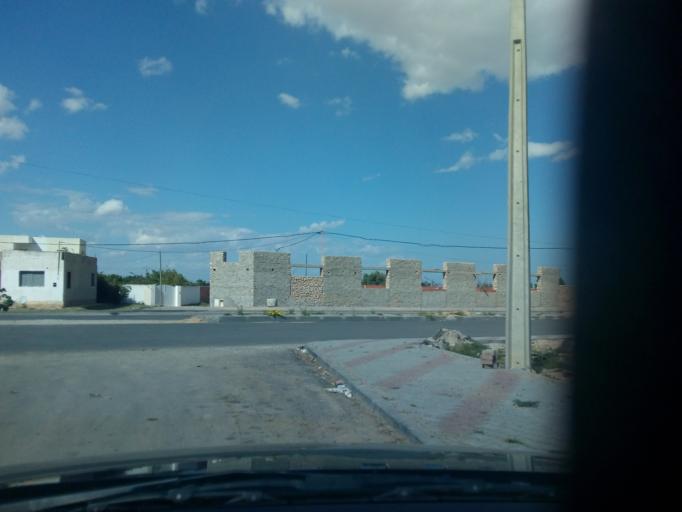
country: TN
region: Safaqis
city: Sfax
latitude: 34.7282
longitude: 10.6113
